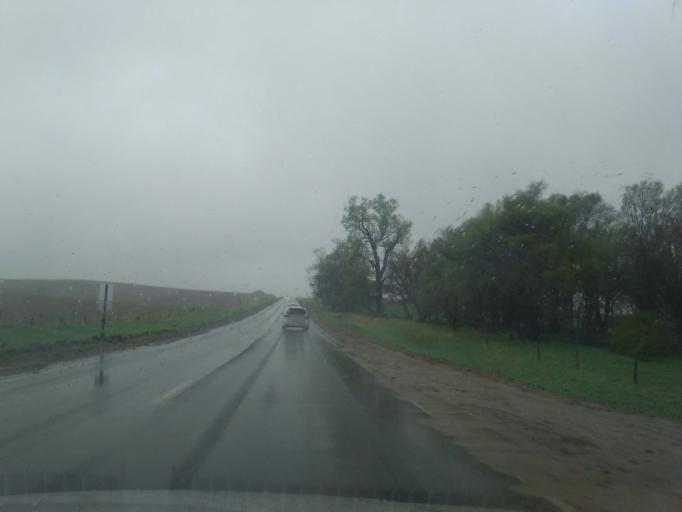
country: US
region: Nebraska
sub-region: Wayne County
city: Wayne
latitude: 42.2205
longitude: -97.1738
